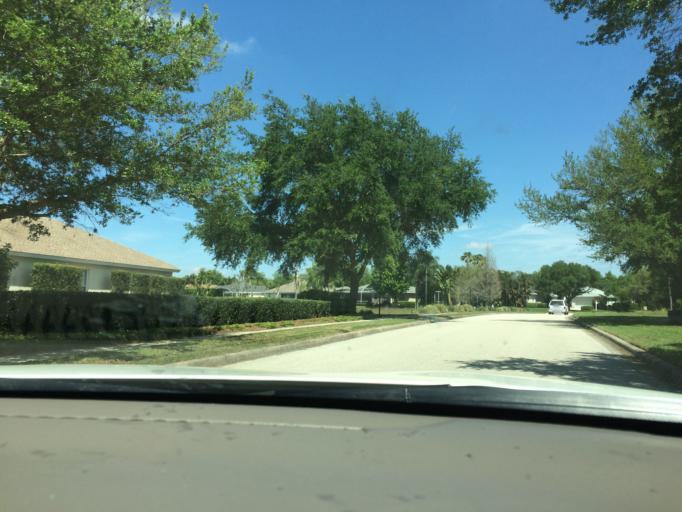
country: US
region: Florida
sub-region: Sarasota County
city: The Meadows
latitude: 27.4248
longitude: -82.4206
